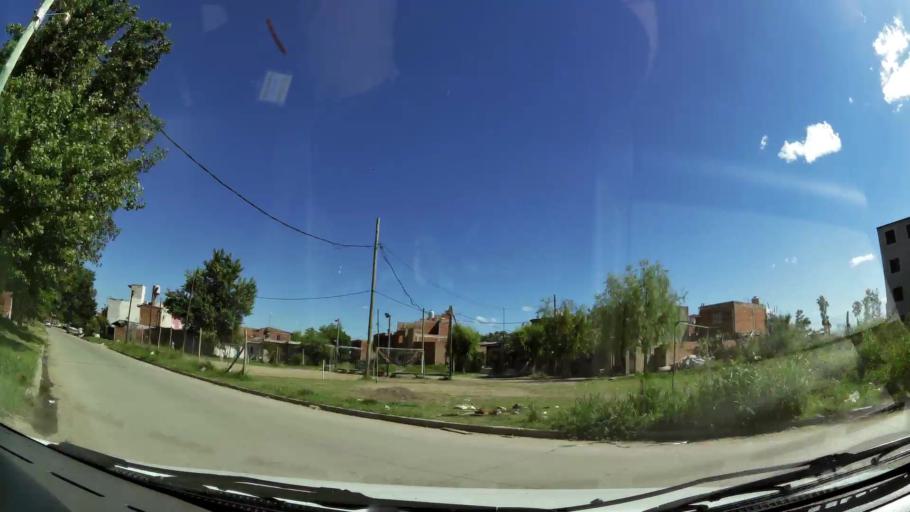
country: AR
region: Buenos Aires
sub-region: Partido de General San Martin
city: General San Martin
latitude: -34.5172
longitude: -58.5852
